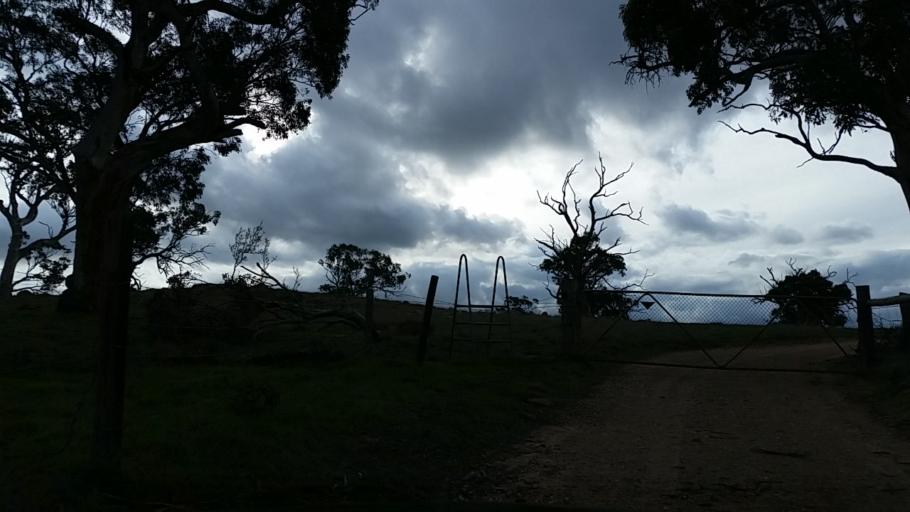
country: AU
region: South Australia
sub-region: Adelaide Hills
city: Birdwood
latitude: -34.9545
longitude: 139.0579
